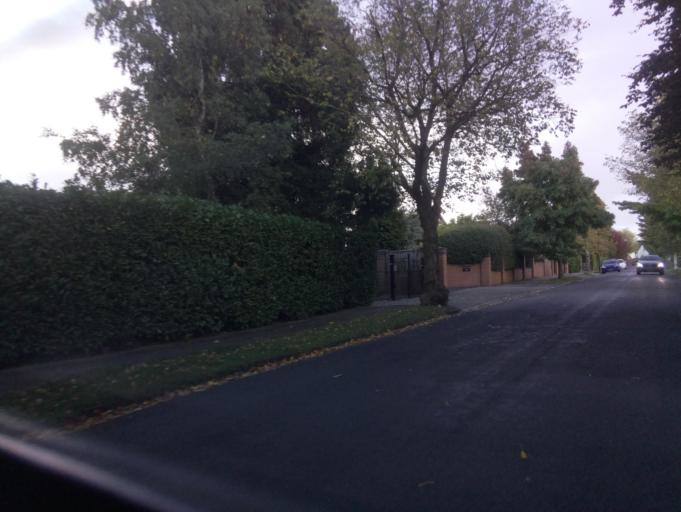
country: GB
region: England
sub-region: Bristol
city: Bristol
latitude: 51.4892
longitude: -2.6115
